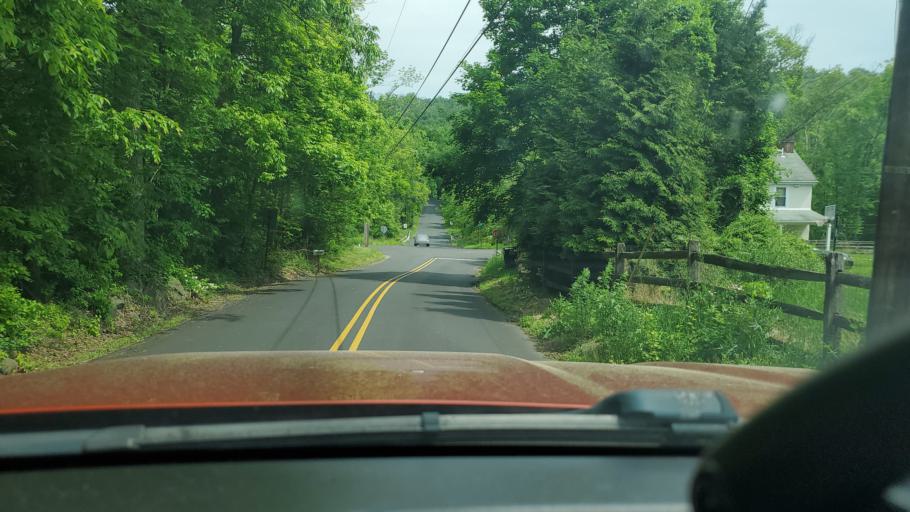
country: US
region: Pennsylvania
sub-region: Montgomery County
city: Red Hill
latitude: 40.3369
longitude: -75.5108
